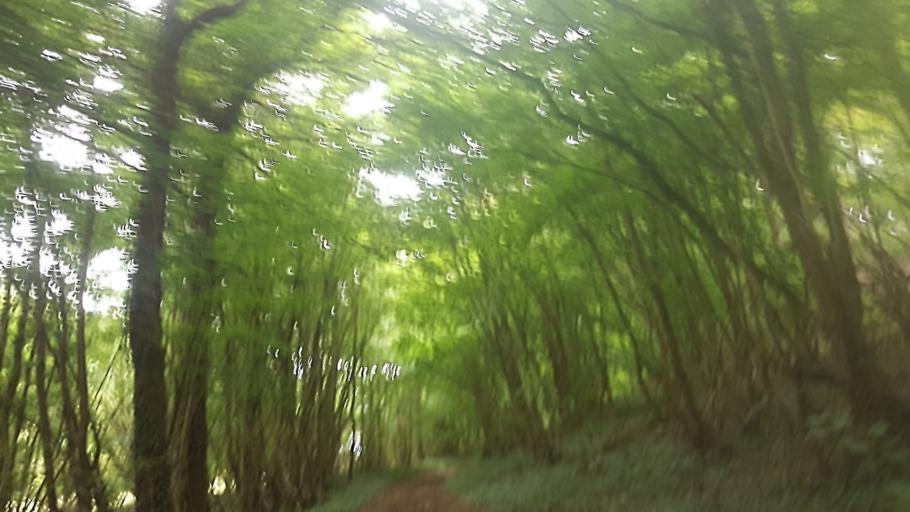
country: BE
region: Wallonia
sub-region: Province de Namur
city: Couvin
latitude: 50.0894
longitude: 4.6017
